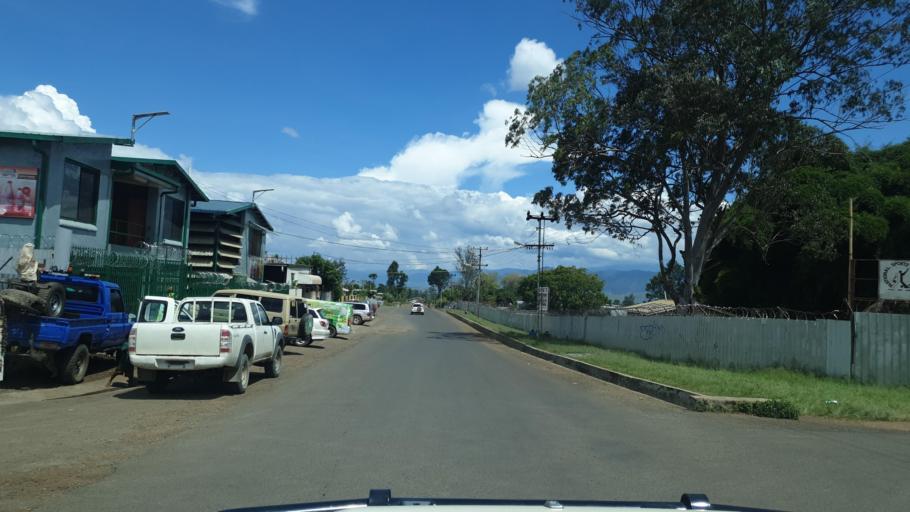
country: PG
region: Eastern Highlands
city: Goroka
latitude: -6.0836
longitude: 145.3878
